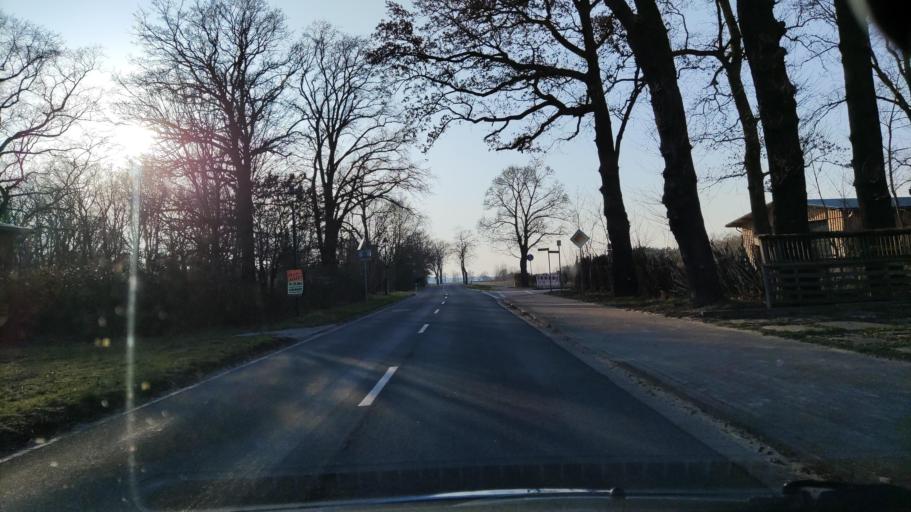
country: DE
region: Brandenburg
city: Lanz
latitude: 52.9930
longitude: 11.5752
